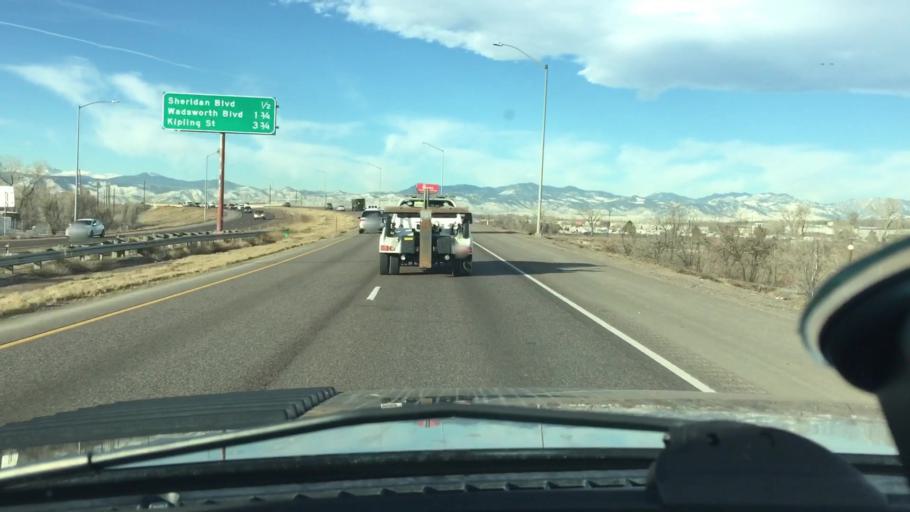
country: US
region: Colorado
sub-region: Adams County
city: Berkley
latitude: 39.7975
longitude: -105.0387
